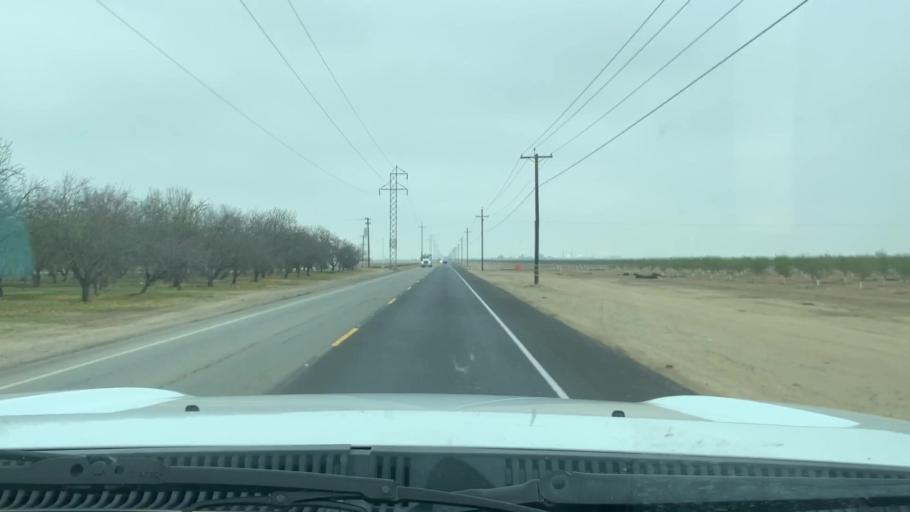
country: US
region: California
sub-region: Kern County
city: Shafter
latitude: 35.4417
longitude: -119.2147
